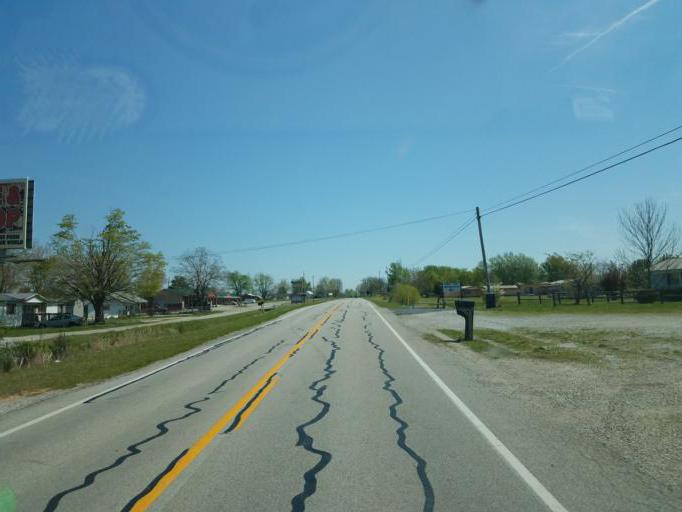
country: US
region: Kentucky
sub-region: Barren County
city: Cave City
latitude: 37.1324
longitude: -86.0204
